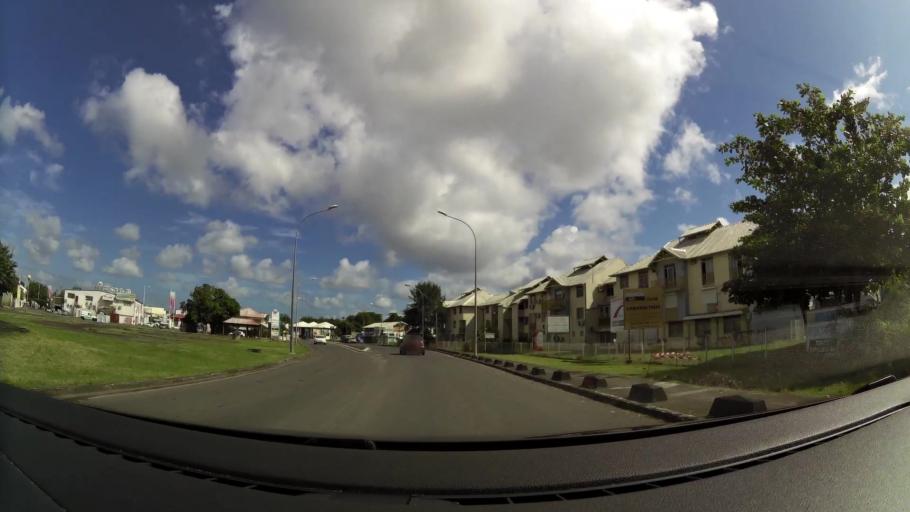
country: GP
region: Guadeloupe
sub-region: Guadeloupe
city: Pointe-a-Pitre
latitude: 16.2491
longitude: -61.5338
